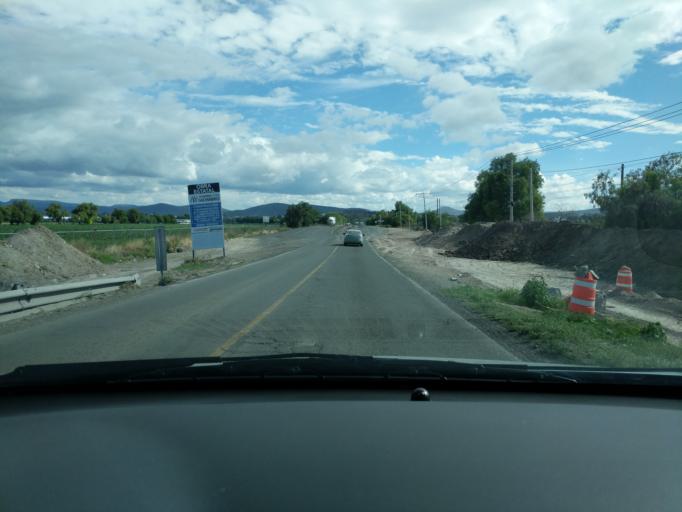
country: MX
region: Queretaro
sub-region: El Marques
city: La Loma
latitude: 20.5907
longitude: -100.2481
